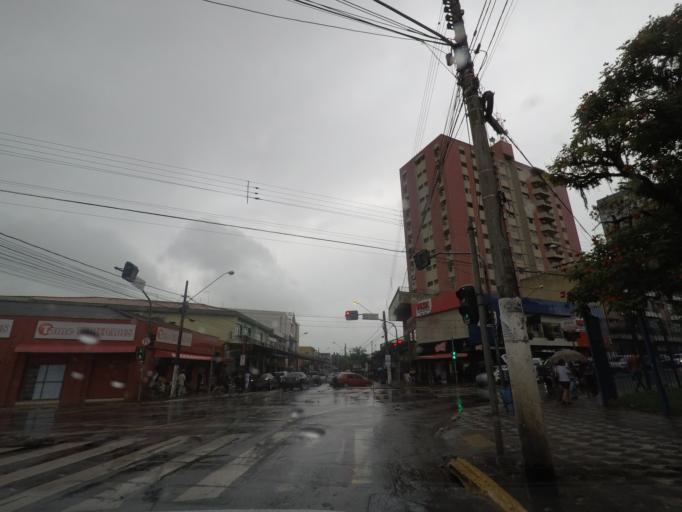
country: BR
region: Sao Paulo
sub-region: Registro
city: Registro
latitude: -24.4953
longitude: -47.8457
